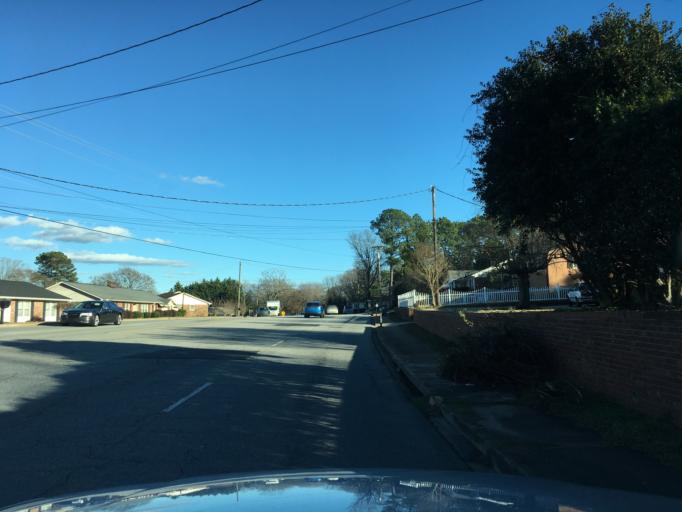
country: US
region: South Carolina
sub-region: Greenville County
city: Wade Hampton
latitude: 34.8723
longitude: -82.3343
